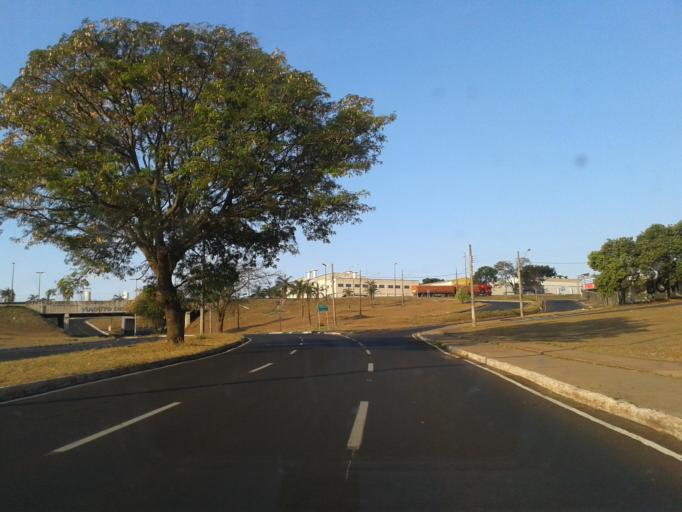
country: BR
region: Minas Gerais
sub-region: Uberlandia
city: Uberlandia
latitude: -18.8947
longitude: -48.2523
